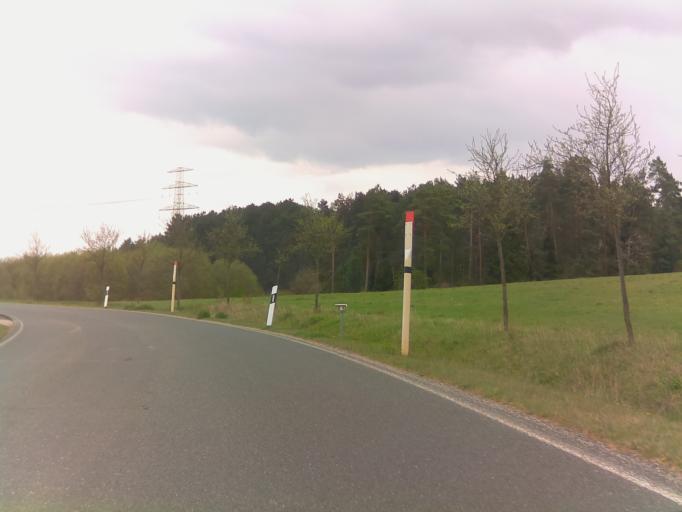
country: DE
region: Thuringia
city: Behringen
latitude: 50.7793
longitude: 11.0024
